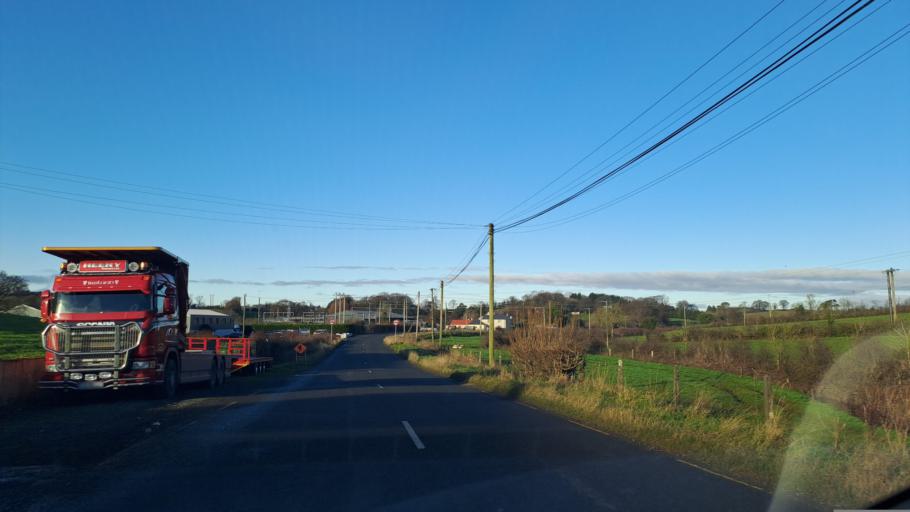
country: IE
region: Ulster
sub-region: An Cabhan
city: Bailieborough
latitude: 53.8942
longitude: -6.9660
